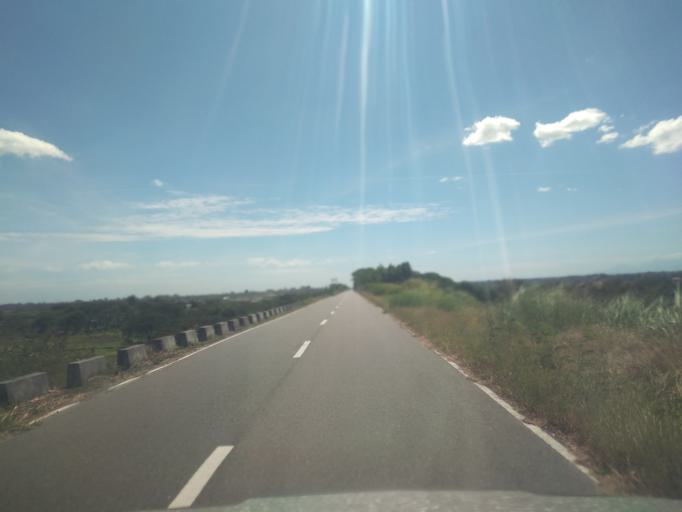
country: PH
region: Central Luzon
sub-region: Province of Pampanga
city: San Basilio
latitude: 15.0286
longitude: 120.5989
